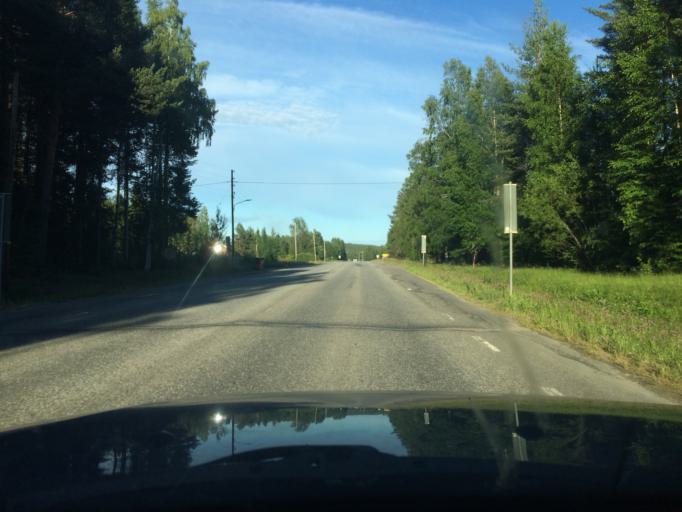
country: SE
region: Norrbotten
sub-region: Pitea Kommun
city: Bergsviken
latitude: 65.3151
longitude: 21.3169
